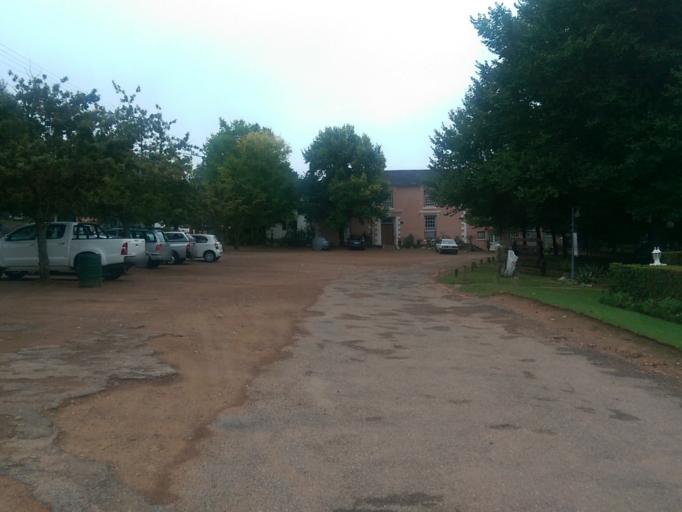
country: ZA
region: Western Cape
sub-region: Overberg District Municipality
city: Swellendam
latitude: -34.0181
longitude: 20.4469
